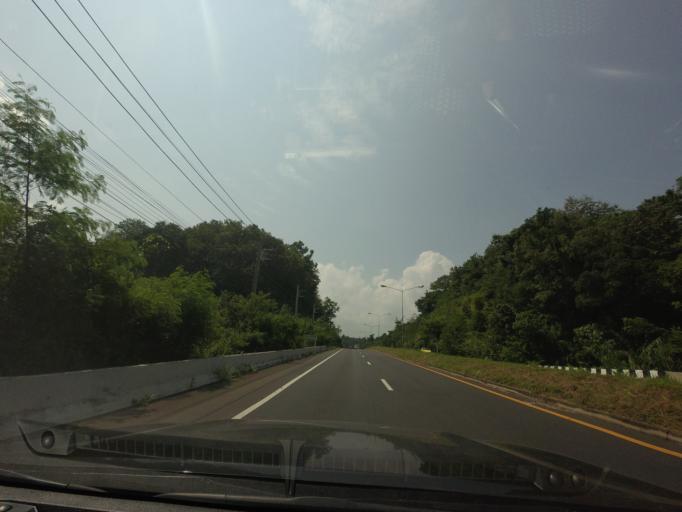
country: TH
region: Phrae
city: Den Chai
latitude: 17.8858
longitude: 100.0482
